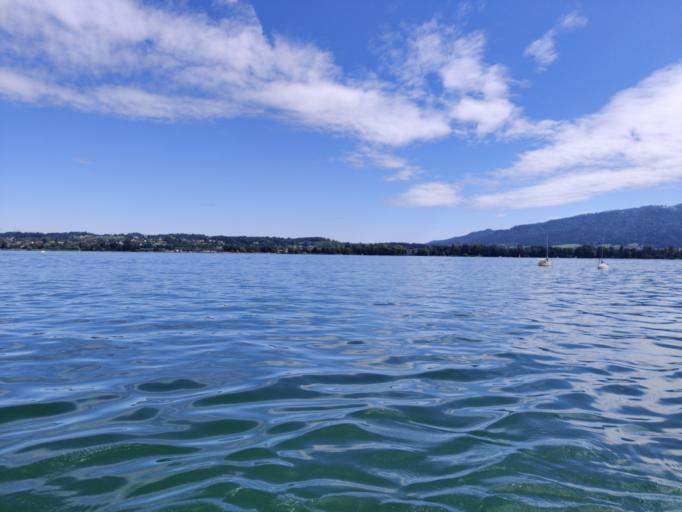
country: DE
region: Bavaria
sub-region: Swabia
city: Lindau
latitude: 47.5355
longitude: 9.7075
